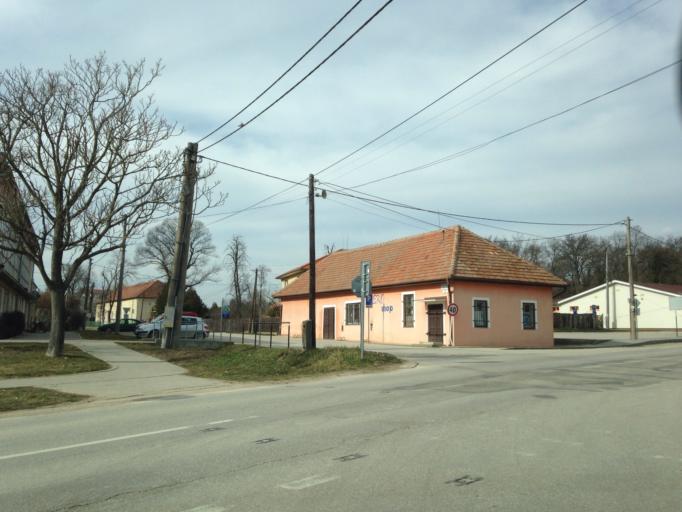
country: SK
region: Nitriansky
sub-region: Okres Komarno
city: Hurbanovo
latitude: 47.8464
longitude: 18.2635
